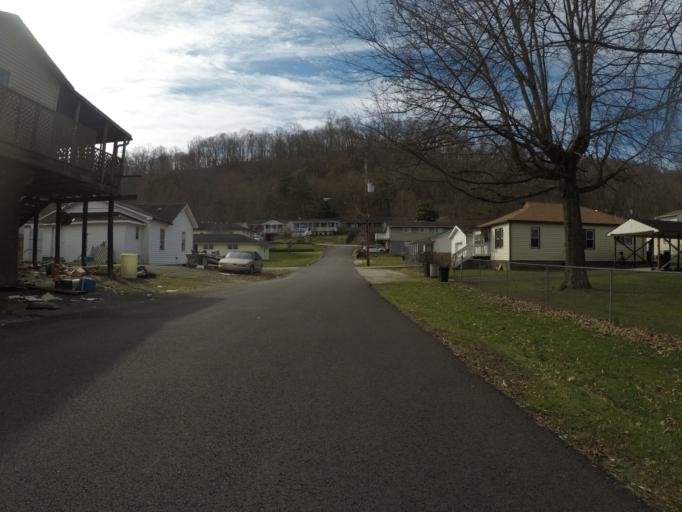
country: US
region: West Virginia
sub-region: Cabell County
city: Barboursville
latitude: 38.4029
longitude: -82.2987
